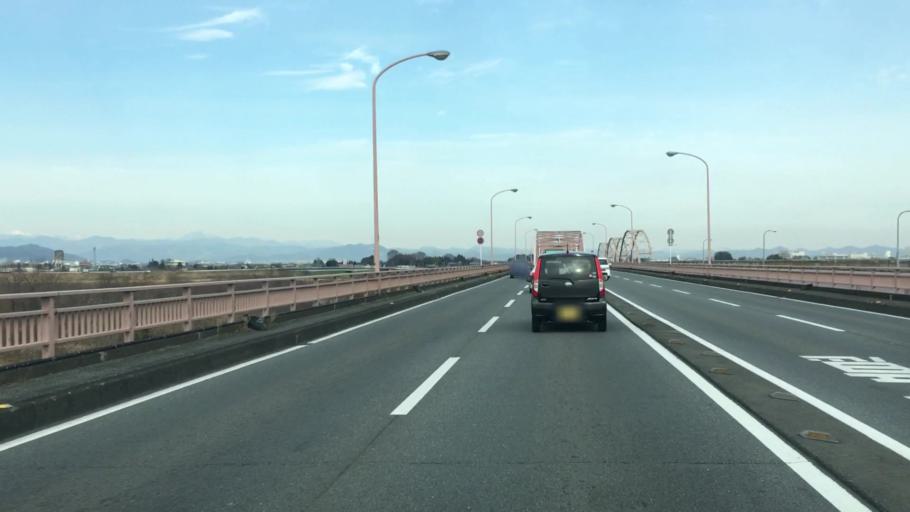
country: JP
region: Saitama
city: Menuma
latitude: 36.2369
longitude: 139.3764
